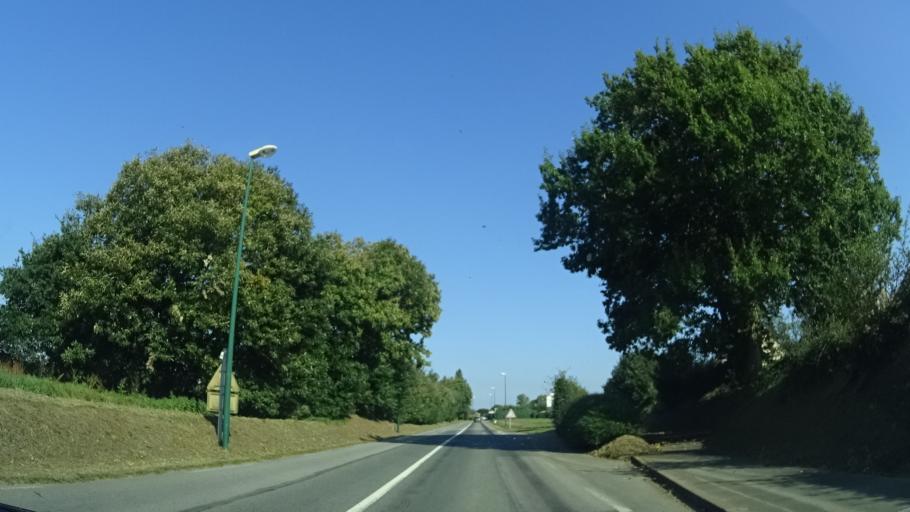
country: FR
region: Brittany
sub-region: Departement du Finistere
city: Plonevez-Porzay
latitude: 48.0913
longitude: -4.2680
